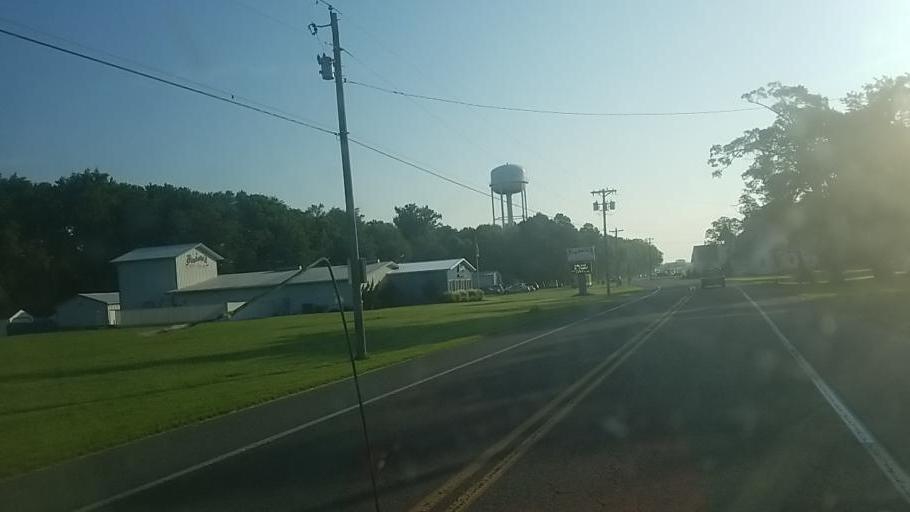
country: US
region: Maryland
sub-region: Worcester County
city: Ocean Pines
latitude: 38.4667
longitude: -75.1208
